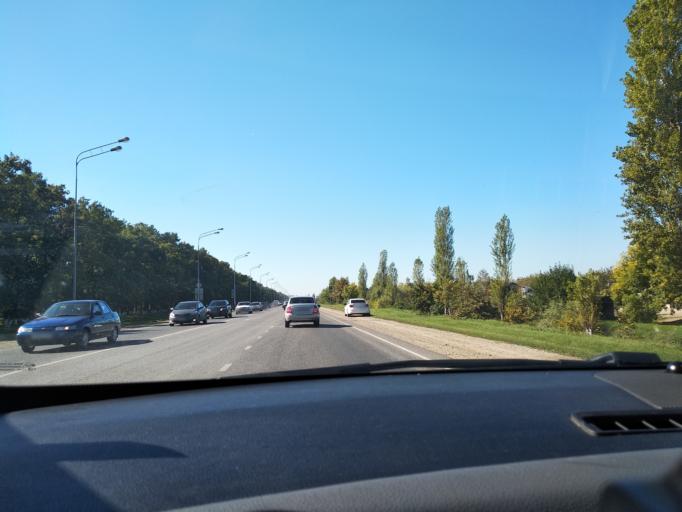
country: RU
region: Krasnodarskiy
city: Novotitarovskaya
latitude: 45.1431
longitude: 39.0438
